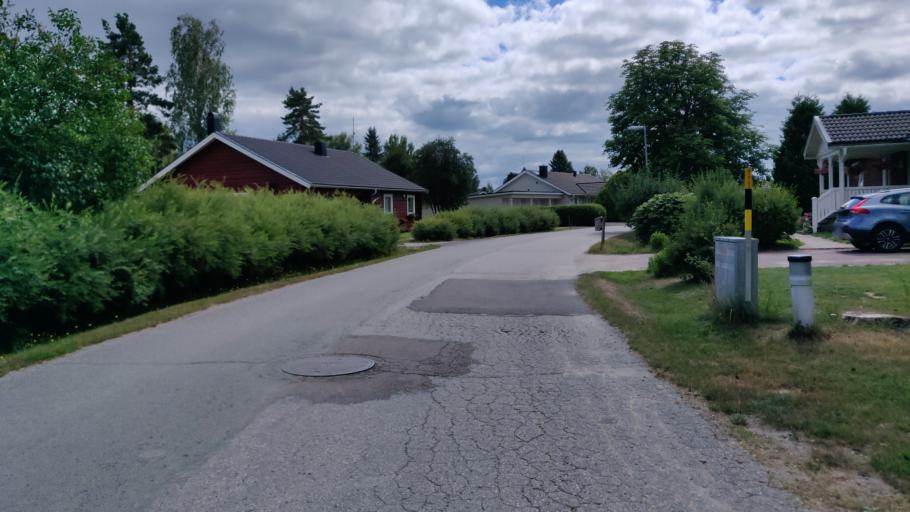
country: SE
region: Vaermland
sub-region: Hagfors Kommun
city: Hagfors
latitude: 60.0012
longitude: 13.5903
